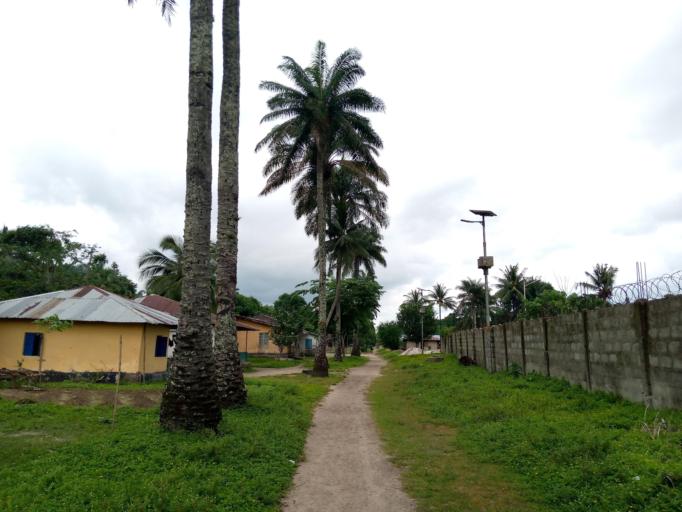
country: SL
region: Southern Province
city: Bonthe
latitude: 7.5299
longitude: -12.5090
